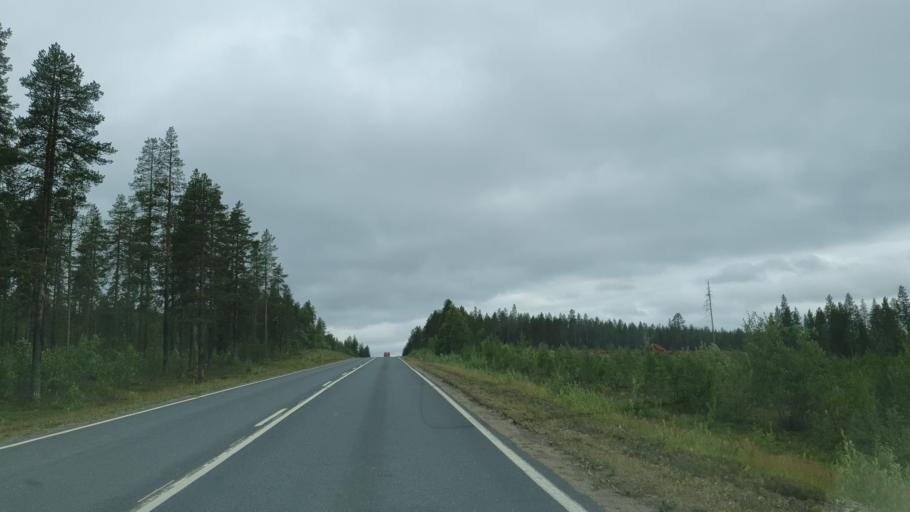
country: FI
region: Lapland
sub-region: Pohjois-Lappi
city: Sodankylae
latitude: 67.4146
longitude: 26.4997
